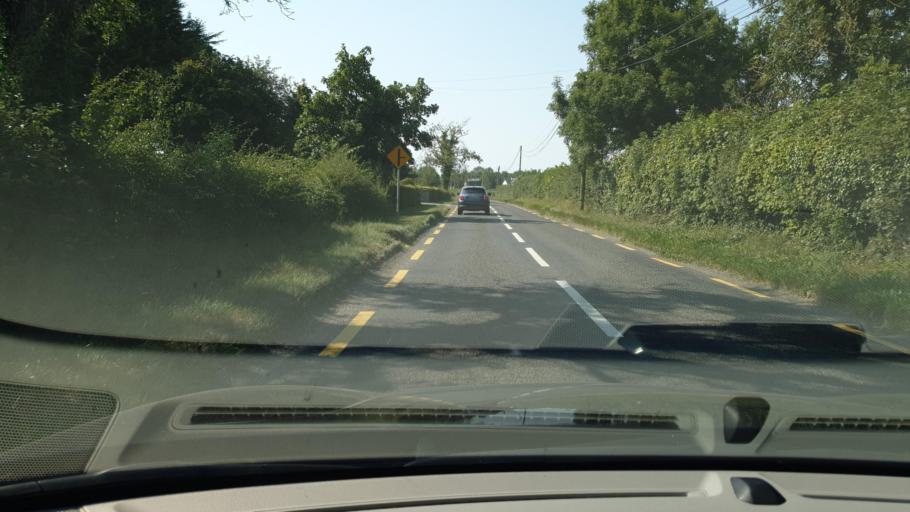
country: IE
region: Leinster
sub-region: An Mhi
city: Trim
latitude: 53.5779
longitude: -6.8367
